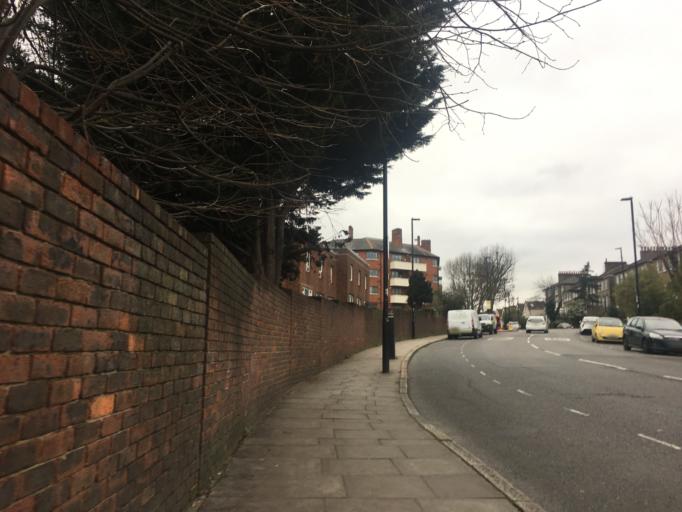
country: GB
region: England
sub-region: Greater London
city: Holloway
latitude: 51.5547
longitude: -0.1353
